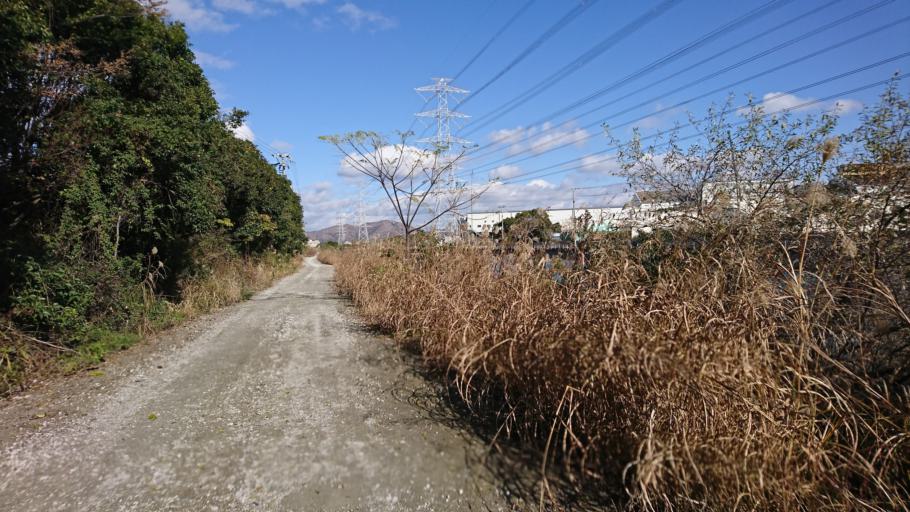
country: JP
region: Hyogo
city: Shirahamacho-usazakiminami
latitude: 34.7615
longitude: 134.7665
